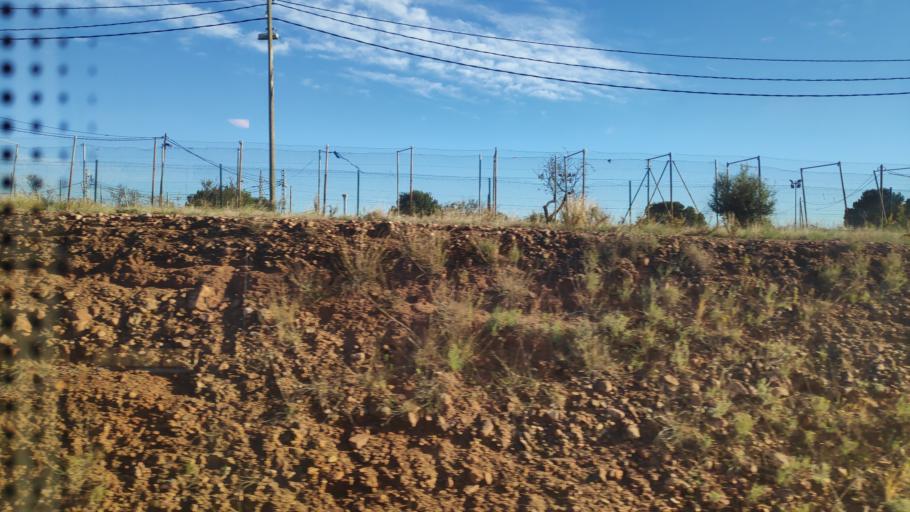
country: ES
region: Valencia
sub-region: Provincia de Castello
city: Benicassim
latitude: 40.0500
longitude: 0.0461
